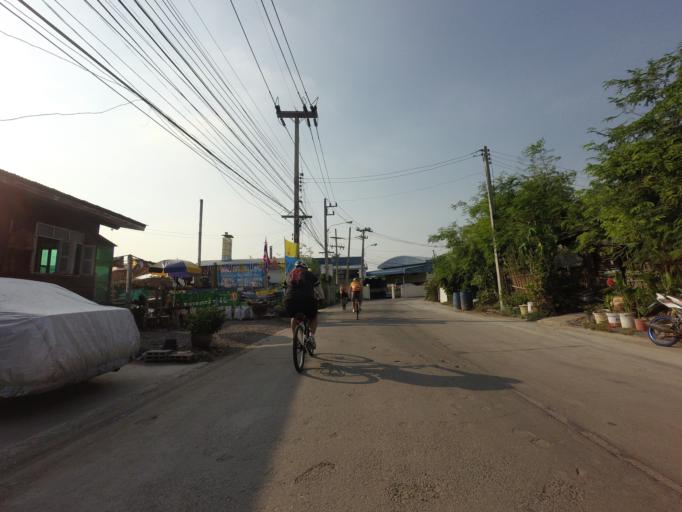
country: TH
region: Samut Sakhon
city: Samut Sakhon
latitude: 13.5141
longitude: 100.2796
